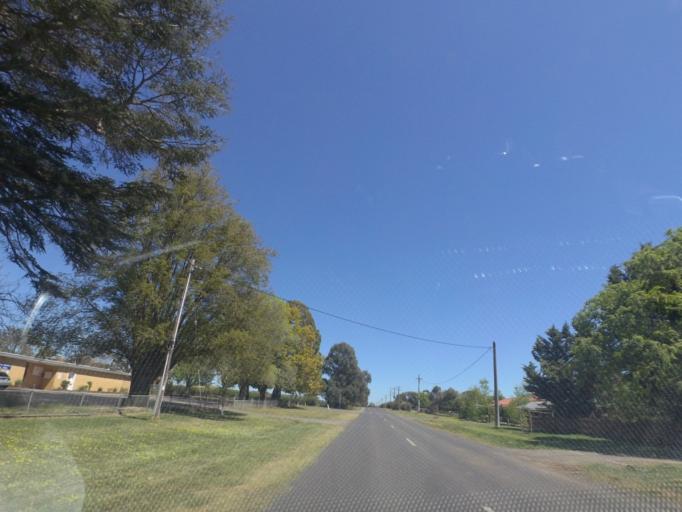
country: AU
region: Victoria
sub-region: Hume
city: Sunbury
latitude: -37.2792
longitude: 144.7232
